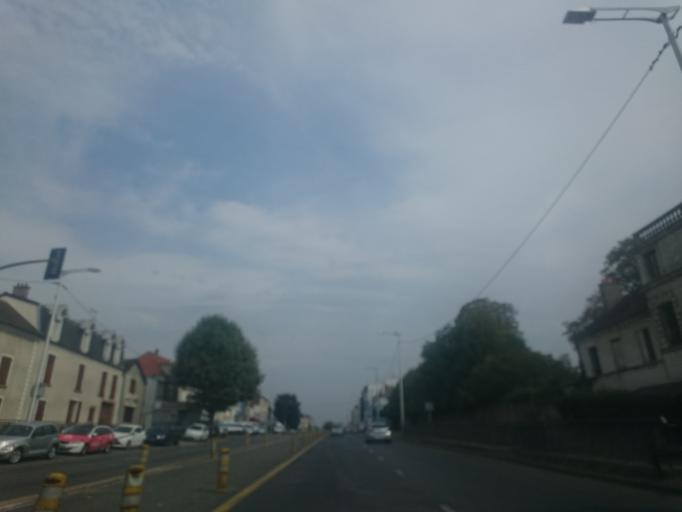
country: FR
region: Ile-de-France
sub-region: Departement de l'Essonne
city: Juvisy-sur-Orge
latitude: 48.6930
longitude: 2.3709
